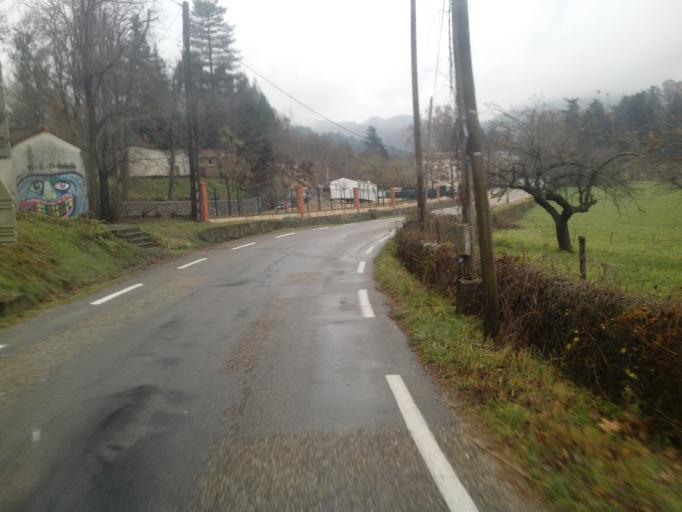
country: FR
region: Languedoc-Roussillon
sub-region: Departement du Gard
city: Lasalle
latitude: 44.0400
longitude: 3.8619
